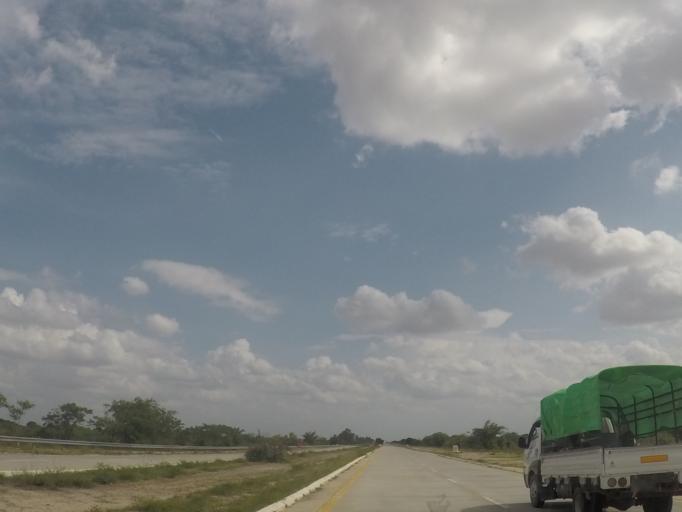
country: MM
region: Mandalay
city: Kyaukse
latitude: 21.4278
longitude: 95.9062
